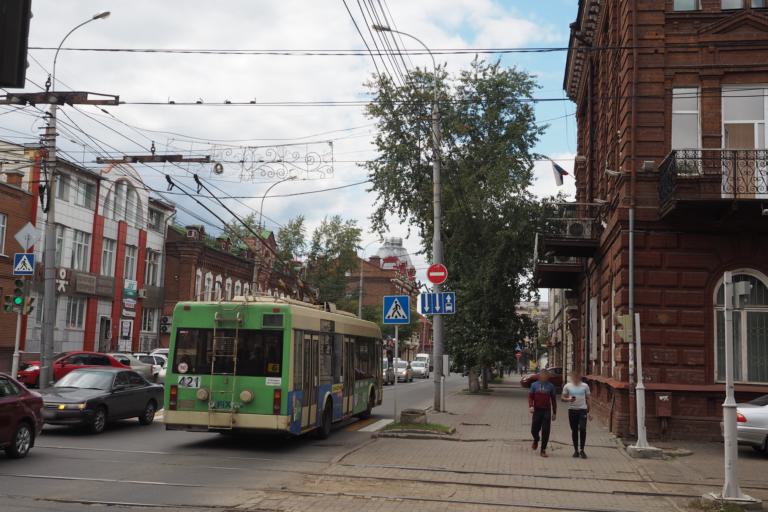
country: RU
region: Tomsk
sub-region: Tomskiy Rayon
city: Tomsk
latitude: 56.4762
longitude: 84.9531
